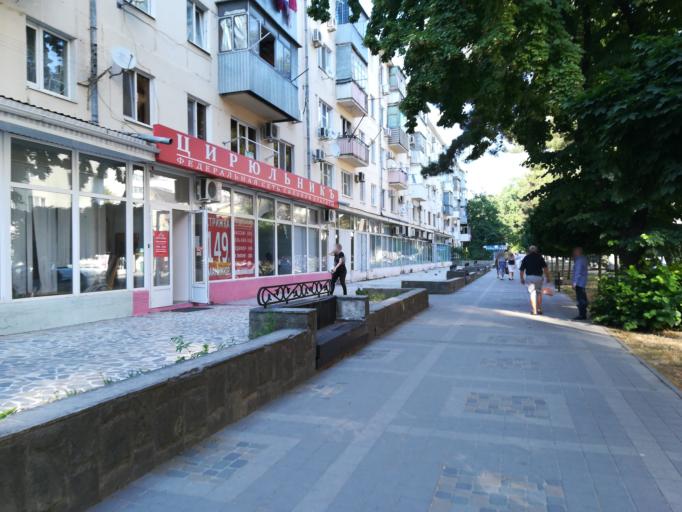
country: RU
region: Krasnodarskiy
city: Anapa
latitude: 44.9001
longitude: 37.3302
